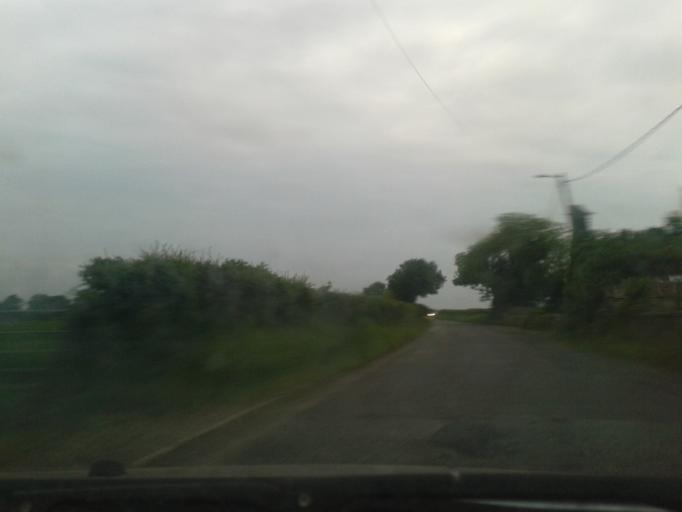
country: IE
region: Leinster
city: Ballymun
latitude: 53.4326
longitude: -6.2645
